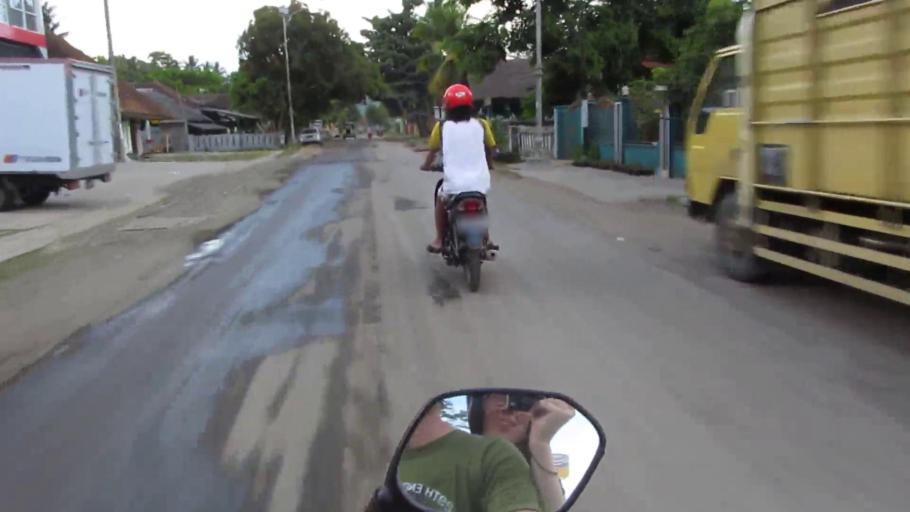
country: ID
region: West Java
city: Binangun
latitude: -7.7210
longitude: 108.4742
